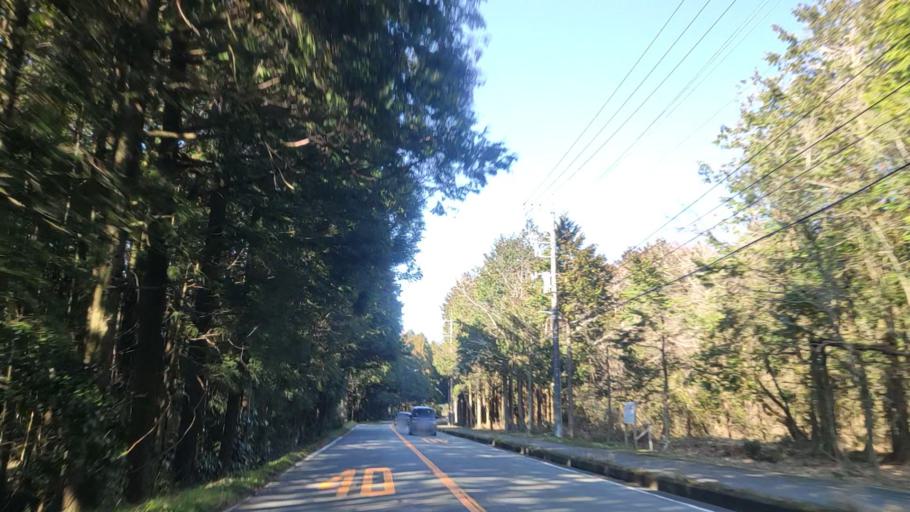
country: JP
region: Shizuoka
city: Fujinomiya
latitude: 35.3232
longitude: 138.5917
